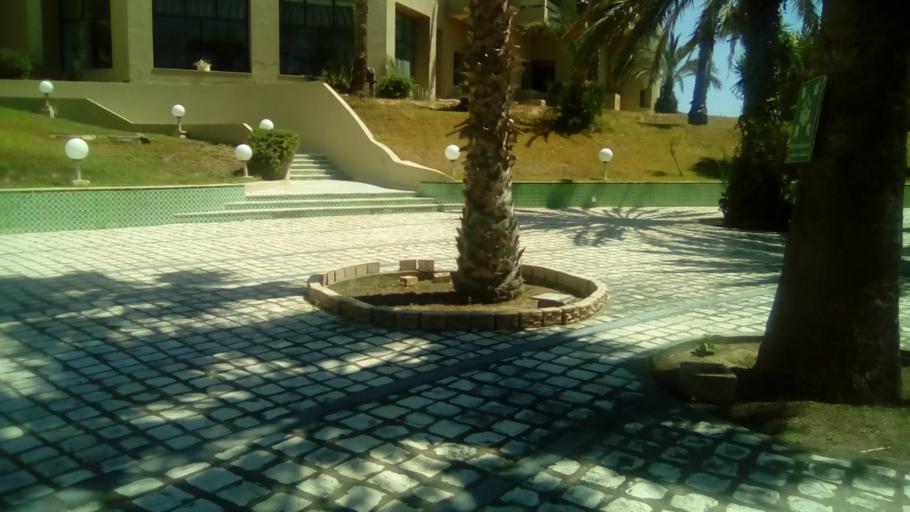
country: TN
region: Nabul
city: Nabeul
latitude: 36.4445
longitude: 10.7371
